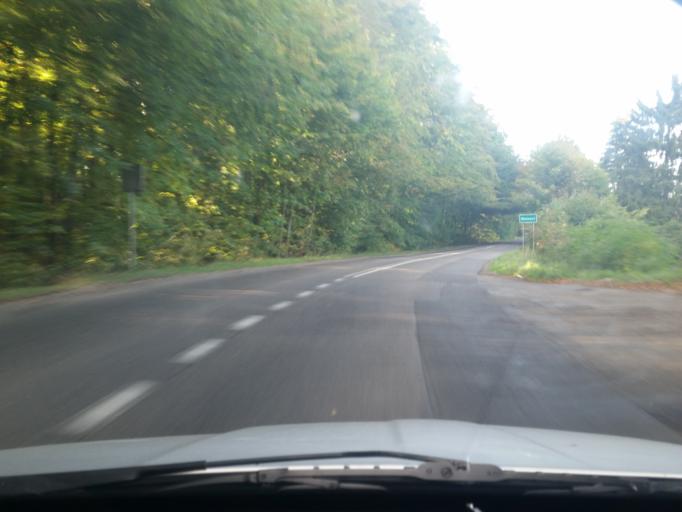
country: PL
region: Pomeranian Voivodeship
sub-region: Powiat chojnicki
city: Chojnice
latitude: 53.7246
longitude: 17.4886
